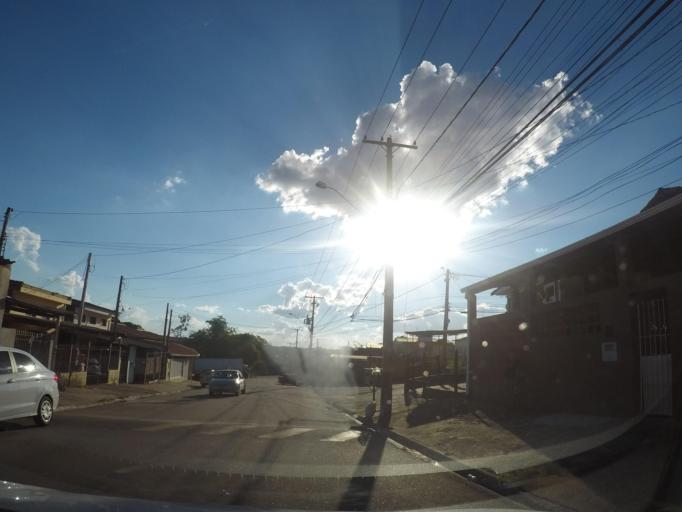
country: BR
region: Sao Paulo
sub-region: Sumare
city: Sumare
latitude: -22.8110
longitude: -47.2282
